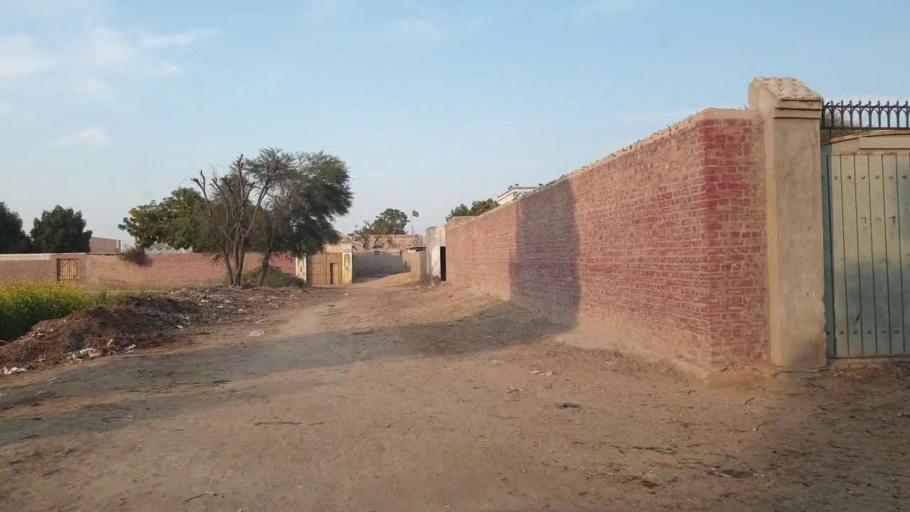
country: PK
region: Sindh
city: Shahpur Chakar
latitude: 26.1626
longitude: 68.6257
